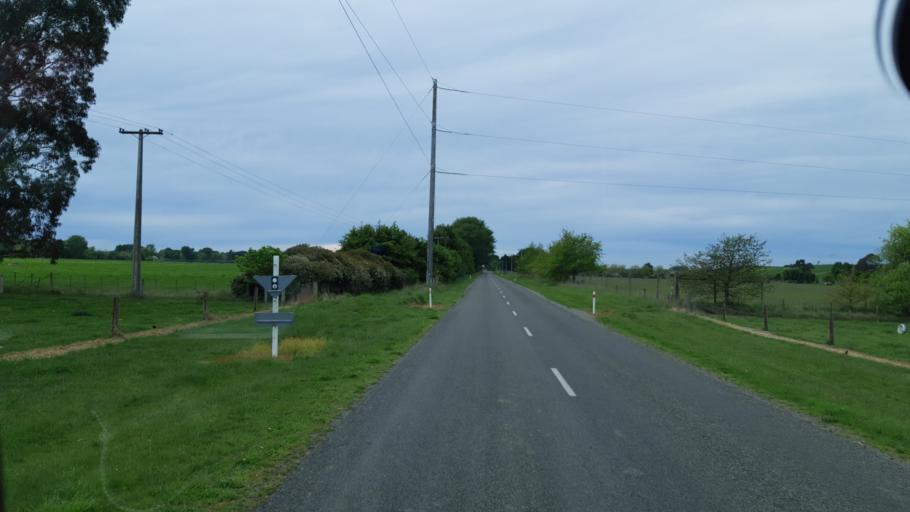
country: NZ
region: Canterbury
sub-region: Timaru District
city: Timaru
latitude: -44.4796
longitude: 171.1468
